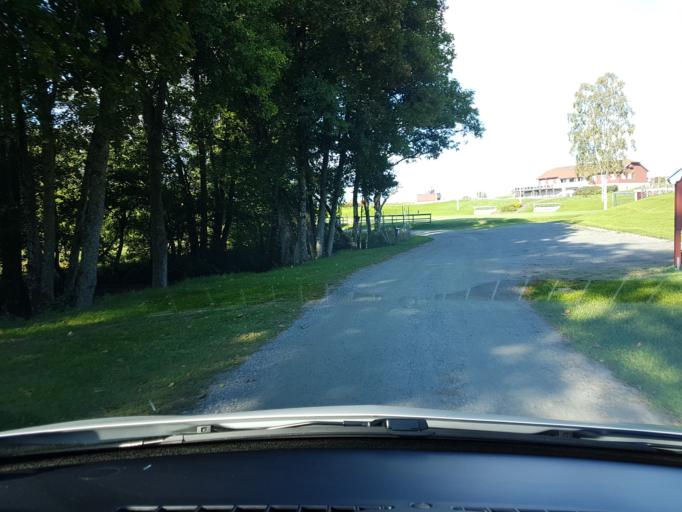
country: SE
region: Vaestra Goetaland
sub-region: Ale Kommun
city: Skepplanda
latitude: 57.9761
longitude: 12.1932
